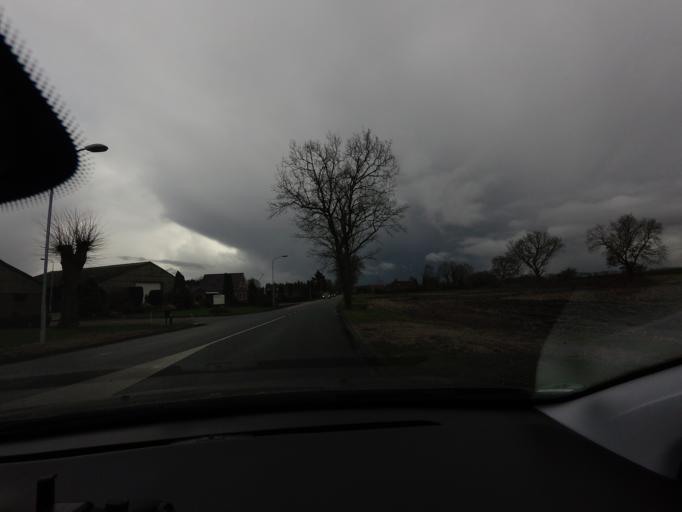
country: NL
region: Drenthe
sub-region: Gemeente Borger-Odoorn
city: Borger
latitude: 52.9948
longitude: 6.7716
